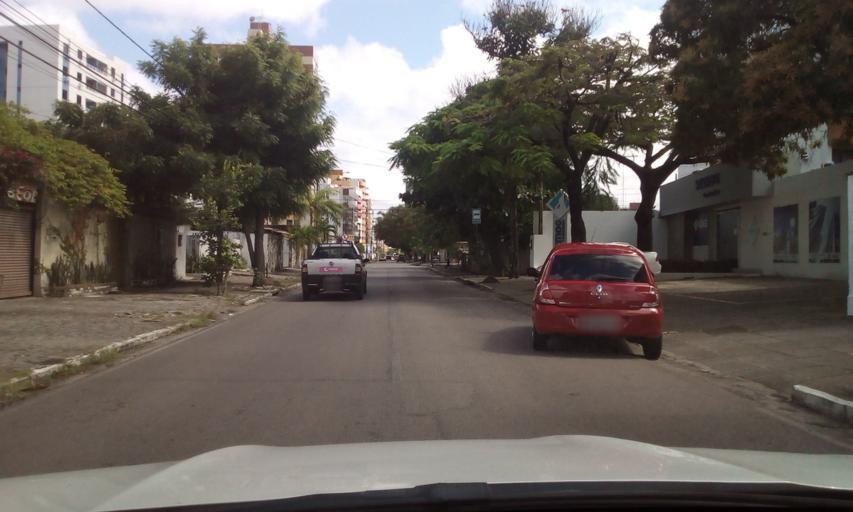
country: BR
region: Paraiba
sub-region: Joao Pessoa
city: Joao Pessoa
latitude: -7.1030
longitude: -34.8332
